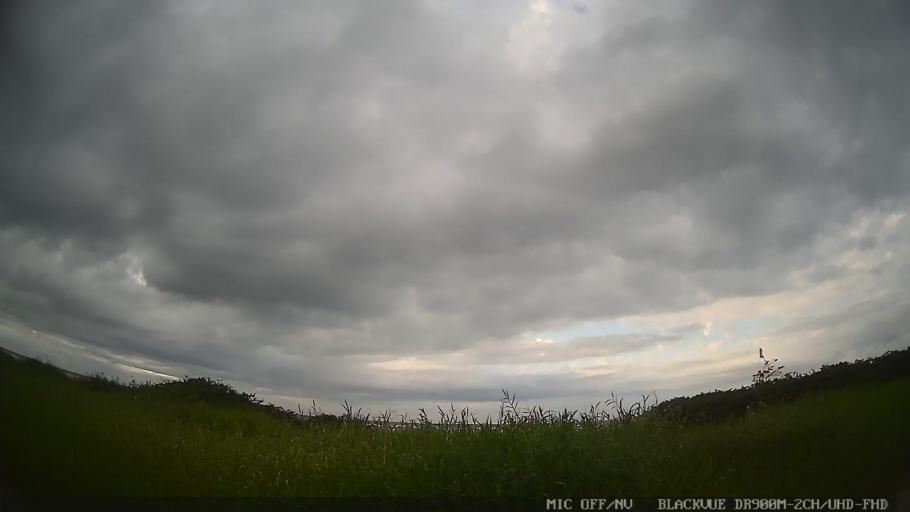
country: BR
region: Sao Paulo
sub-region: Itanhaem
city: Itanhaem
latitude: -24.2294
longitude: -46.8648
